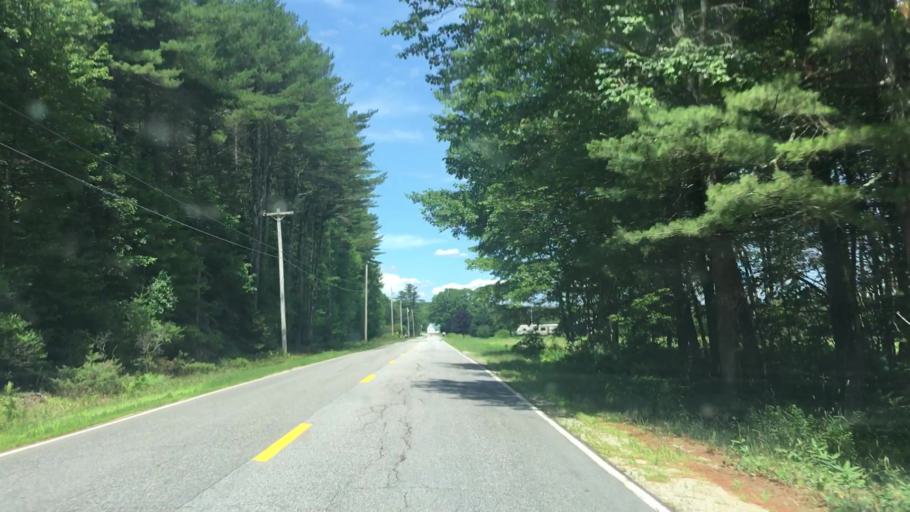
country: US
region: Maine
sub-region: Androscoggin County
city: Livermore
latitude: 44.3459
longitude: -70.1920
